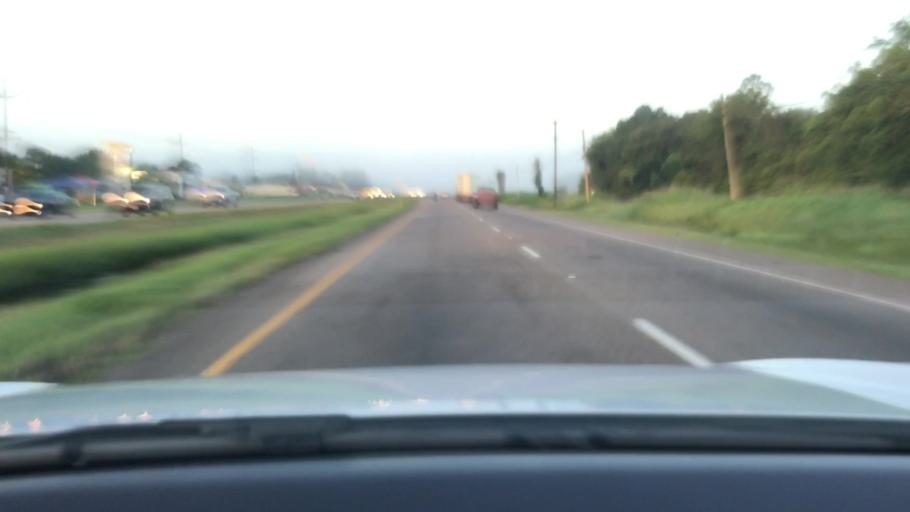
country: US
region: Louisiana
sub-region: West Baton Rouge Parish
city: Brusly
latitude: 30.4104
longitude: -91.2276
